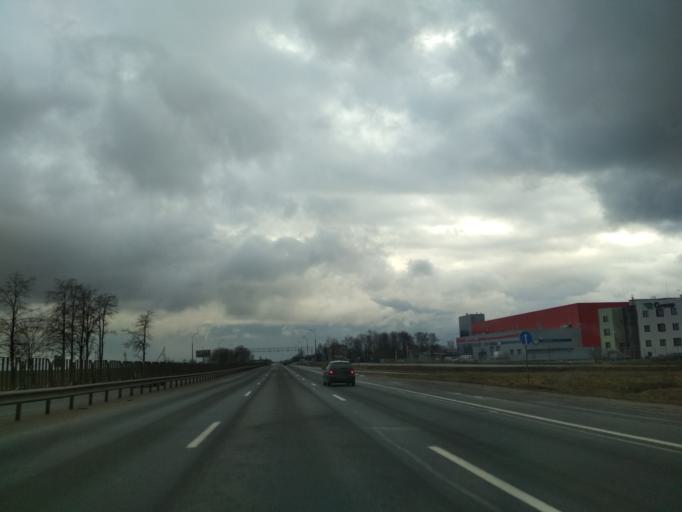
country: BY
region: Minsk
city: Pryvol'ny
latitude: 53.8034
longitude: 27.7964
